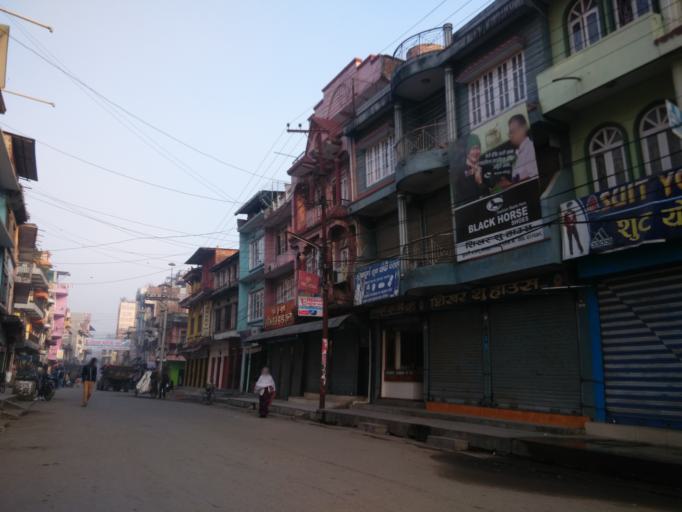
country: NP
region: Central Region
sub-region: Narayani Zone
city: Bharatpur
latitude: 27.6975
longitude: 84.4248
